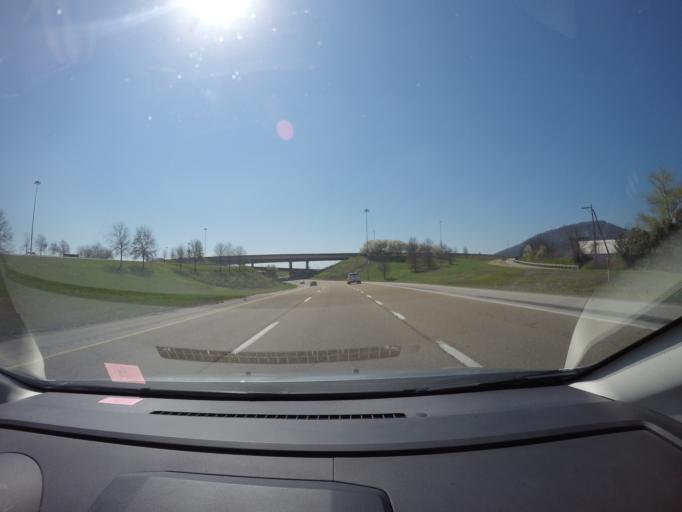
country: US
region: Tennessee
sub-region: Hamilton County
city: Chattanooga
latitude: 35.0340
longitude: -85.3193
